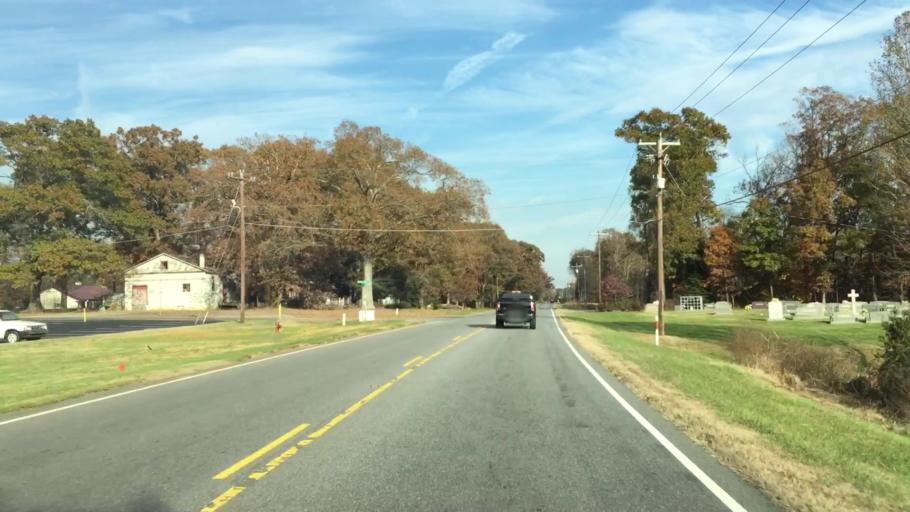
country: US
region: North Carolina
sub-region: Guilford County
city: Summerfield
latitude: 36.2539
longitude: -79.8931
